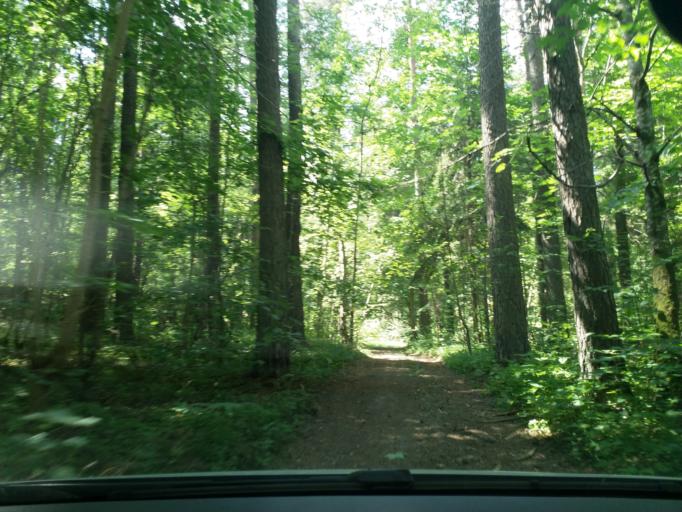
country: LV
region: Kuldigas Rajons
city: Kuldiga
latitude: 56.9697
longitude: 21.9244
